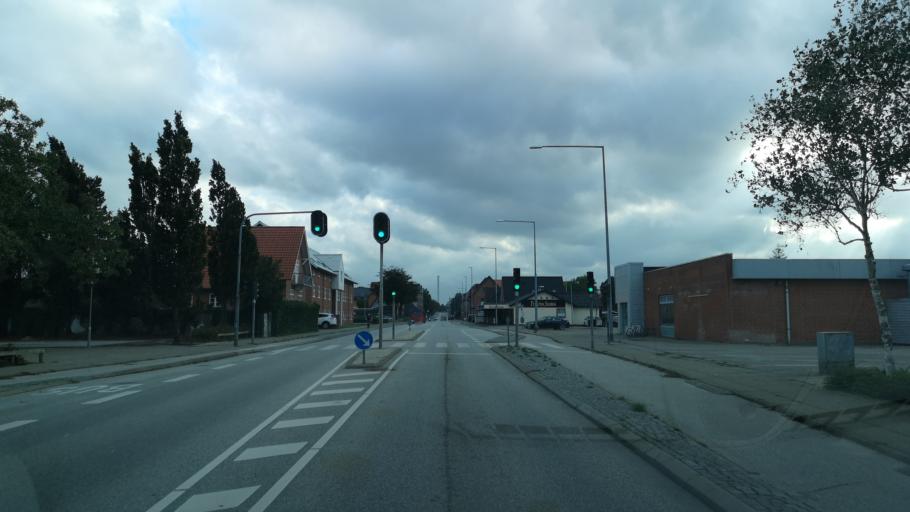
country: DK
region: Central Jutland
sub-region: Herning Kommune
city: Herning
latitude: 56.1413
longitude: 8.9915
